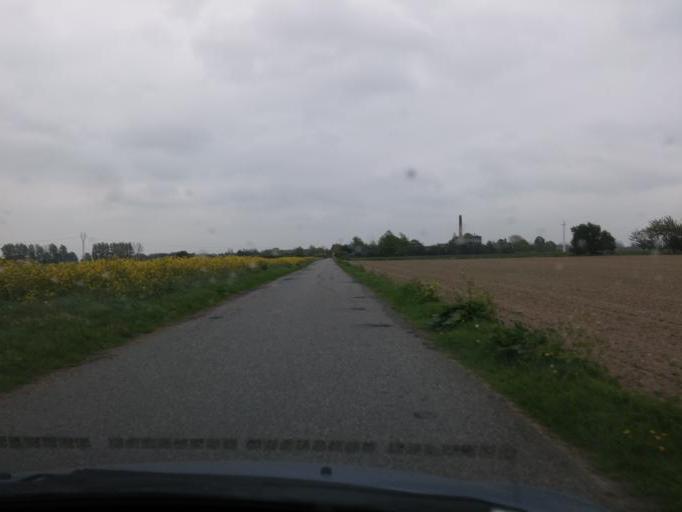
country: DK
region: South Denmark
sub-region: Odense Kommune
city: Bullerup
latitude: 55.4066
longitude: 10.5229
